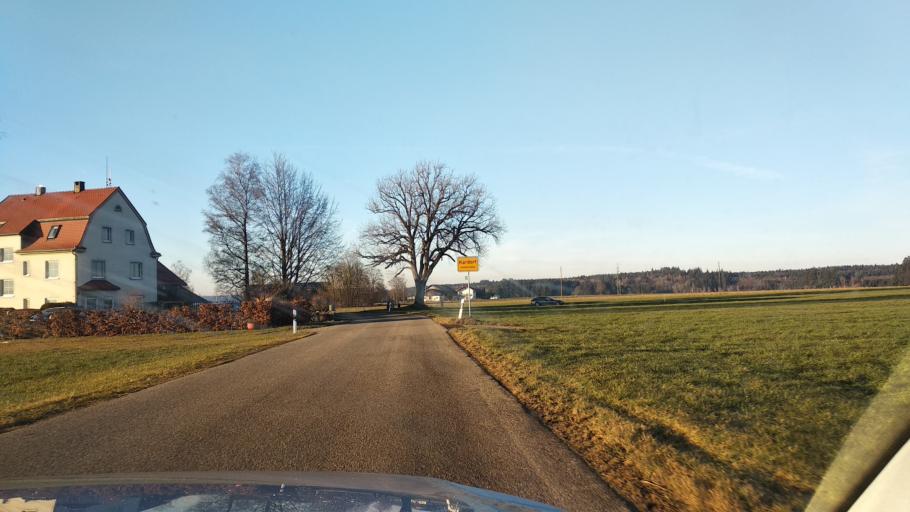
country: DE
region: Bavaria
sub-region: Swabia
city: Lautrach
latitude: 47.9193
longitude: 10.1281
